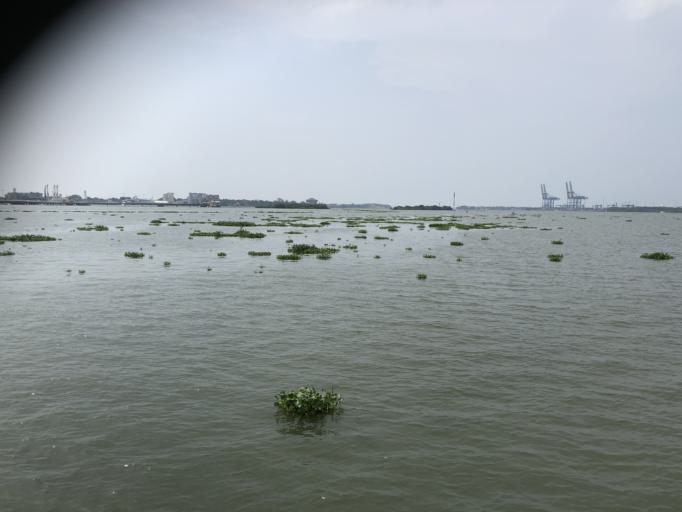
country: IN
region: Kerala
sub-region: Ernakulam
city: Cochin
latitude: 9.9776
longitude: 76.2754
